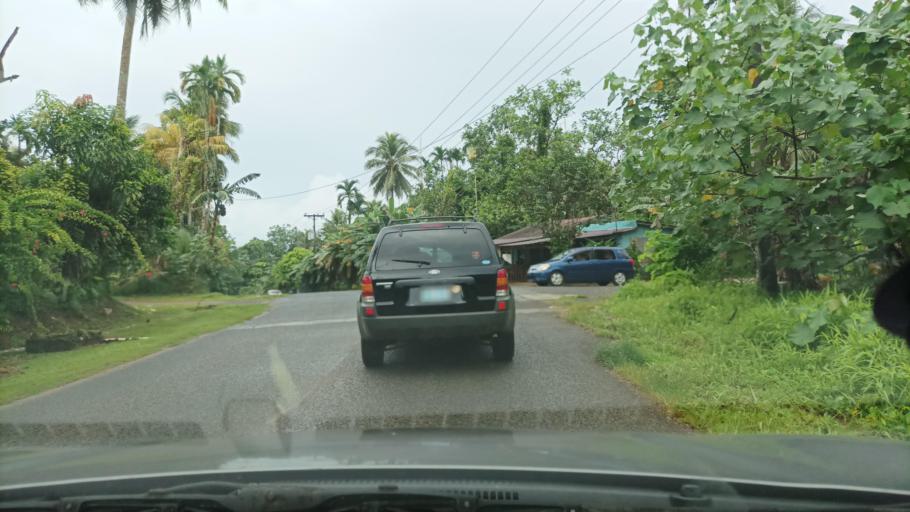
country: FM
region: Pohnpei
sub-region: Sokehs Municipality
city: Palikir - National Government Center
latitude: 6.9016
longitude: 158.1569
